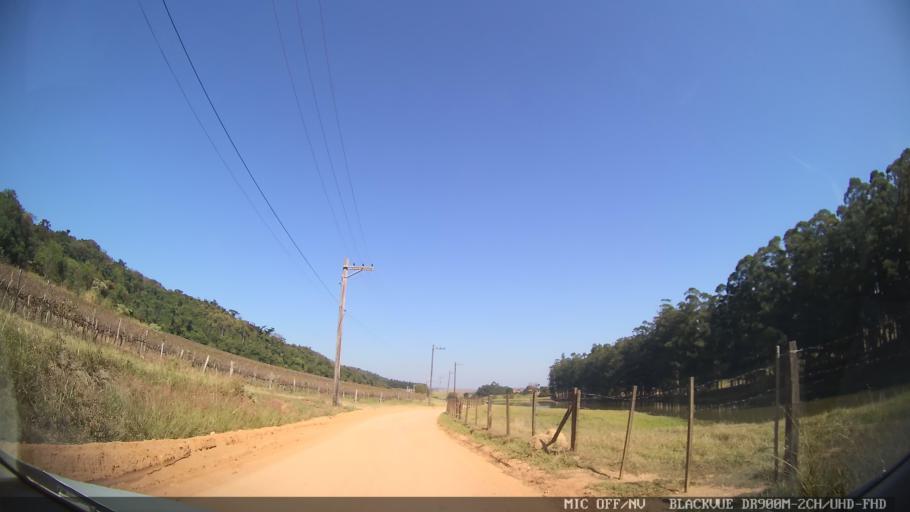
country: BR
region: Sao Paulo
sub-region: Itupeva
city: Itupeva
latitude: -23.1131
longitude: -47.0617
